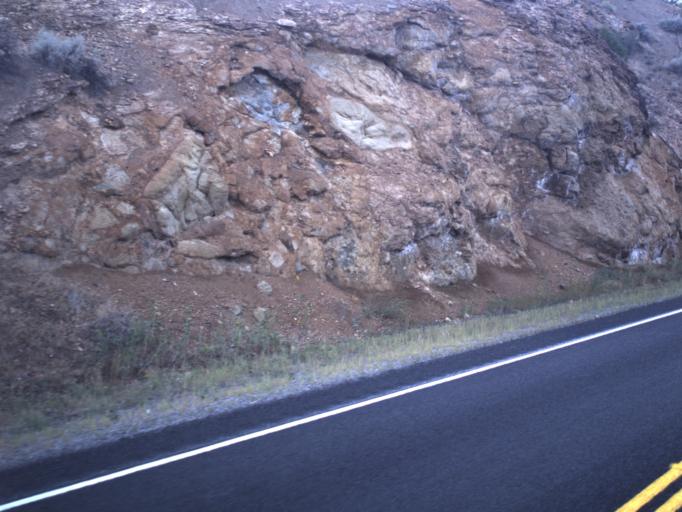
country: US
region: Utah
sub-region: Sevier County
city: Monroe
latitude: 38.5507
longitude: -112.2689
